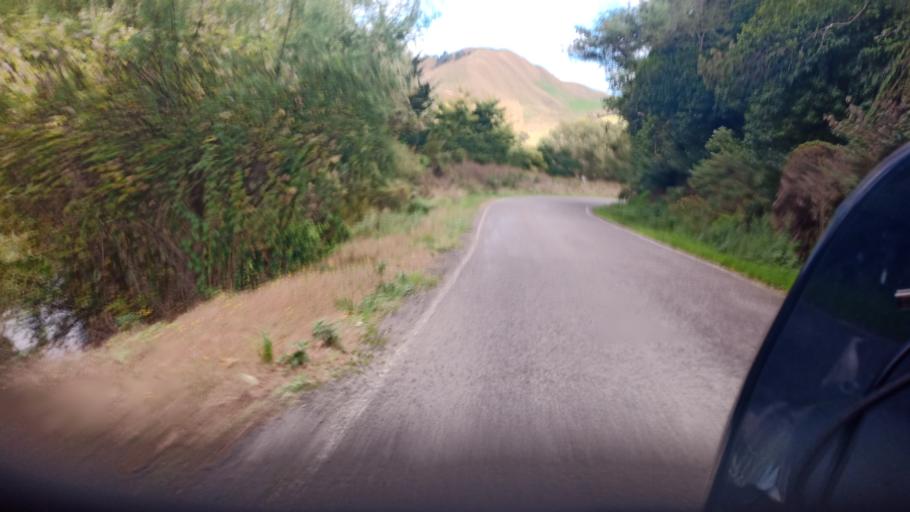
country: NZ
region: Gisborne
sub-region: Gisborne District
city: Gisborne
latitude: -38.4318
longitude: 177.7409
